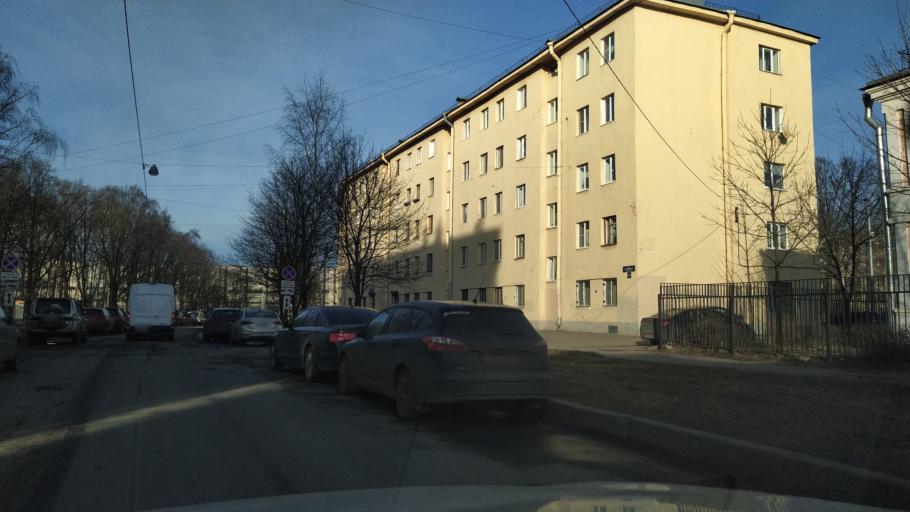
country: RU
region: St.-Petersburg
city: Kupchino
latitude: 59.8774
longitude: 30.3312
